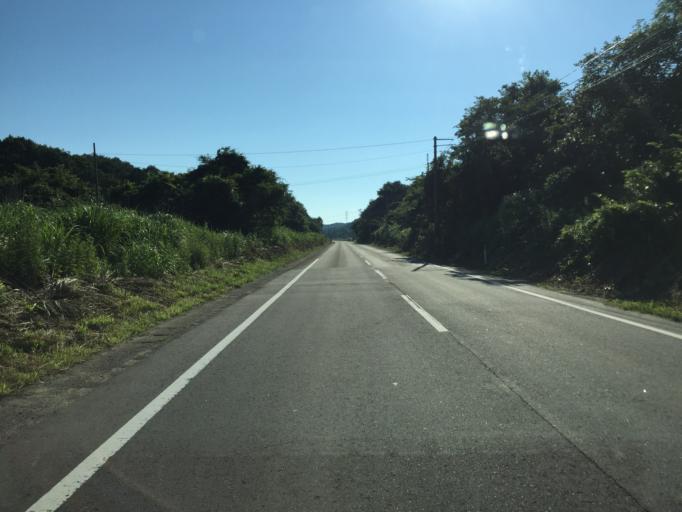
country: JP
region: Fukushima
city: Yanagawamachi-saiwaicho
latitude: 37.7574
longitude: 140.7185
